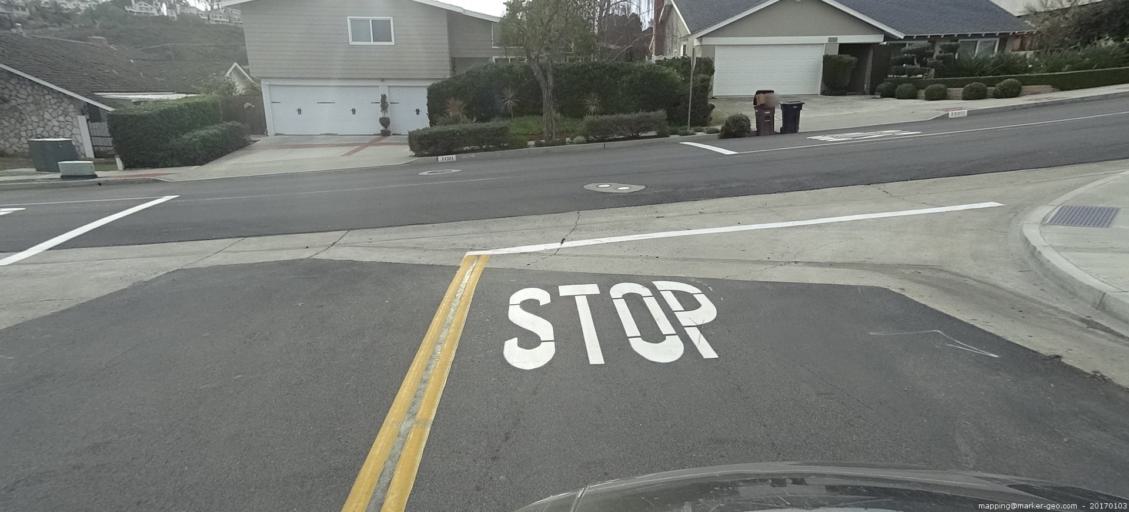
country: US
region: California
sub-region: Orange County
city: Dana Point
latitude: 33.4789
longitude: -117.6914
